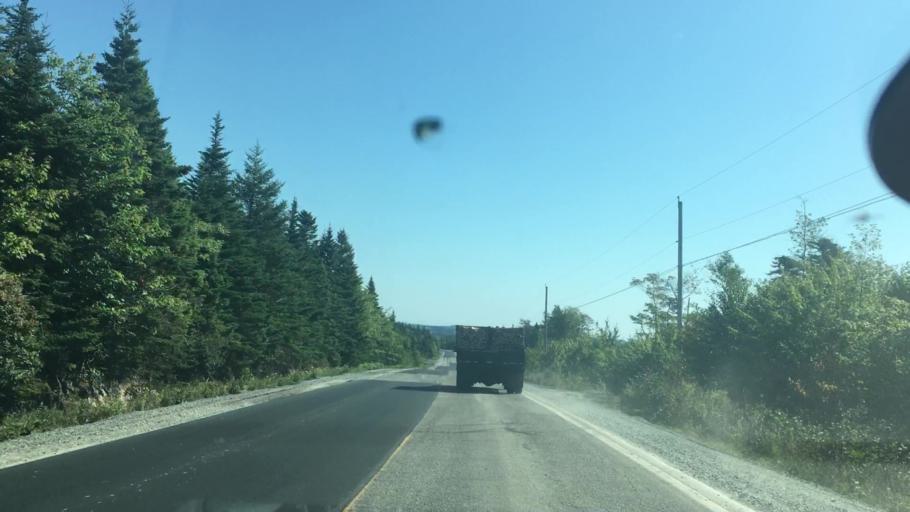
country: CA
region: Nova Scotia
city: New Glasgow
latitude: 44.8982
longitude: -62.4303
